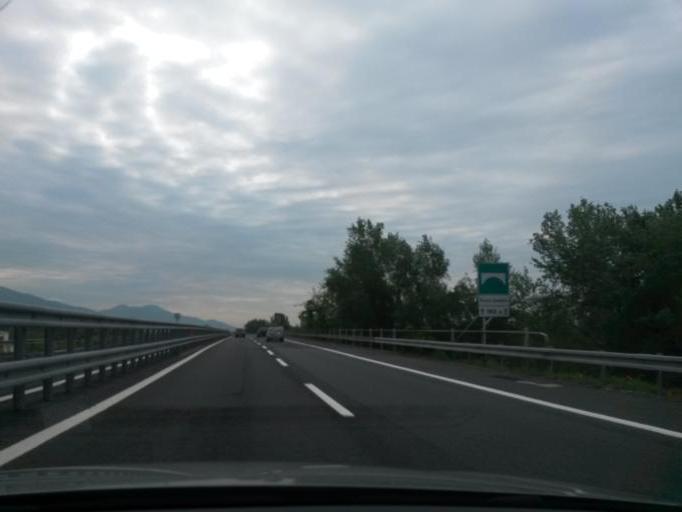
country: IT
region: Tuscany
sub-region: Provincia di Massa-Carrara
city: Carrara
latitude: 44.0363
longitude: 10.0676
